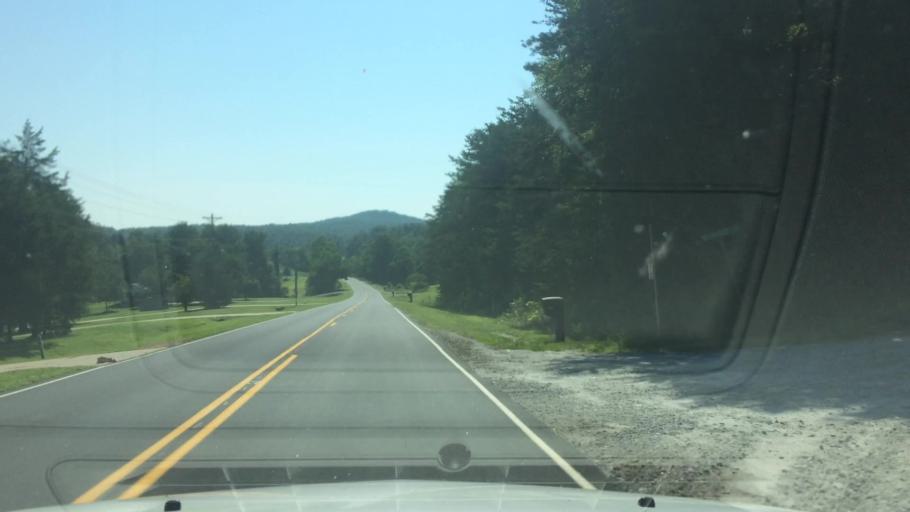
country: US
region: North Carolina
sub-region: Caldwell County
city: Sawmills
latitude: 35.9070
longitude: -81.3965
